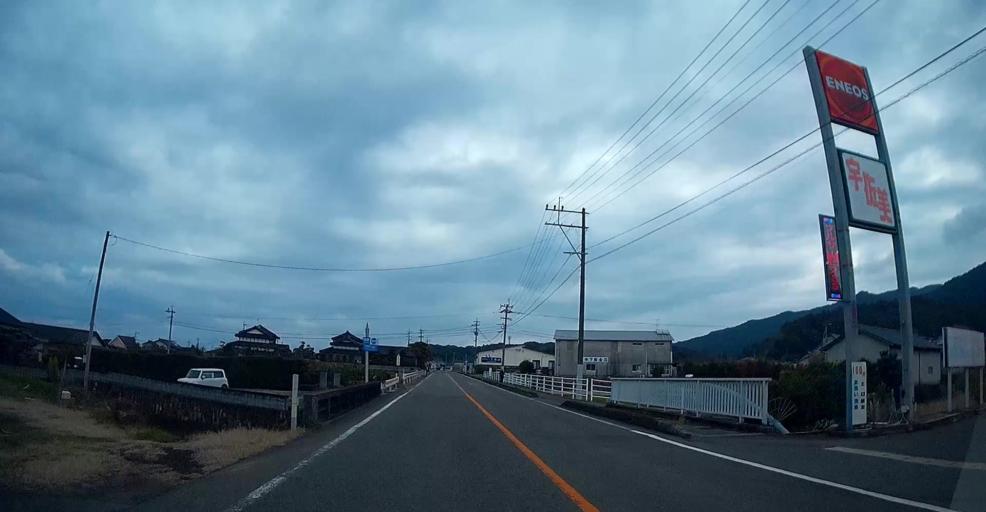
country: JP
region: Kumamoto
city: Hondo
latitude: 32.4723
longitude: 130.2550
